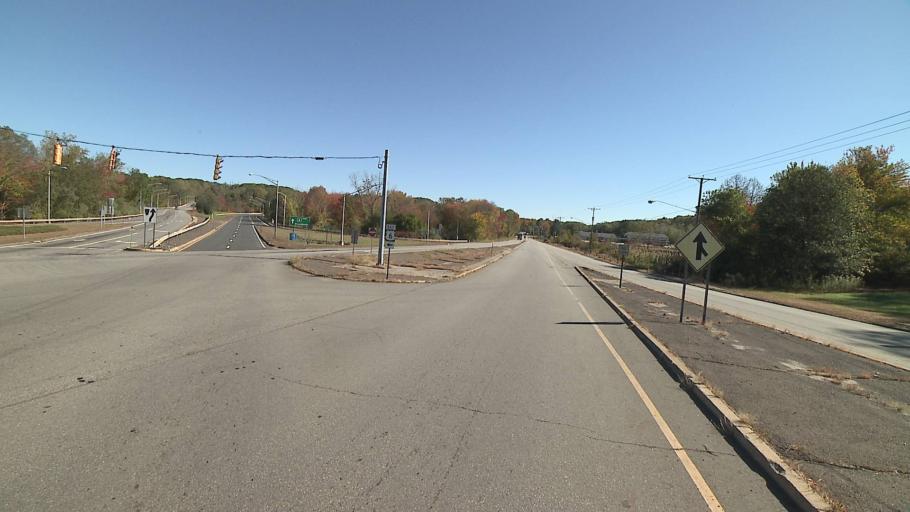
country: US
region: Connecticut
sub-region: Tolland County
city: South Coventry
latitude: 41.7193
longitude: -72.2788
